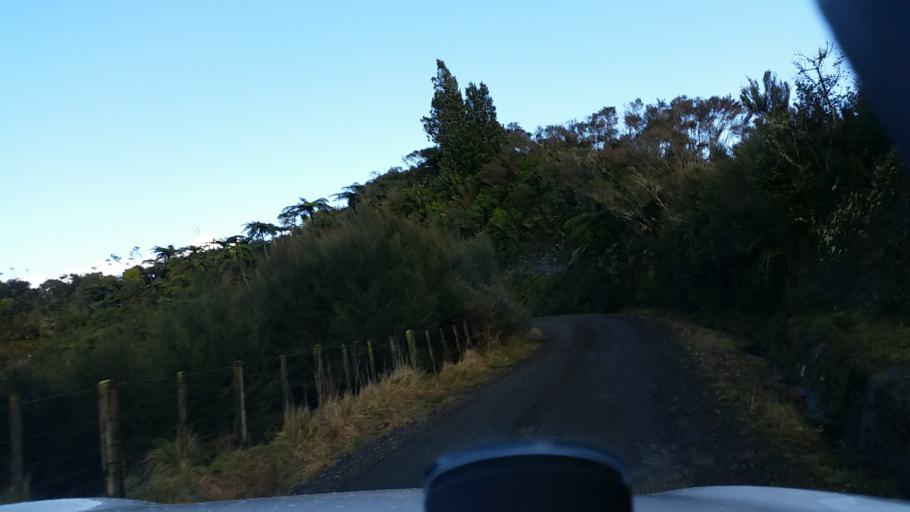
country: NZ
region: Taranaki
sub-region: South Taranaki District
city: Eltham
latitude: -39.4183
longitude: 174.5568
